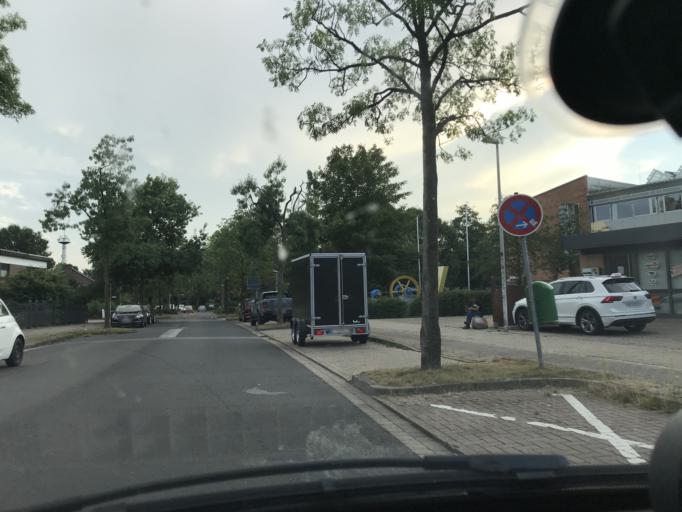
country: DE
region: Lower Saxony
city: Buxtehude
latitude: 53.4788
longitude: 9.6963
